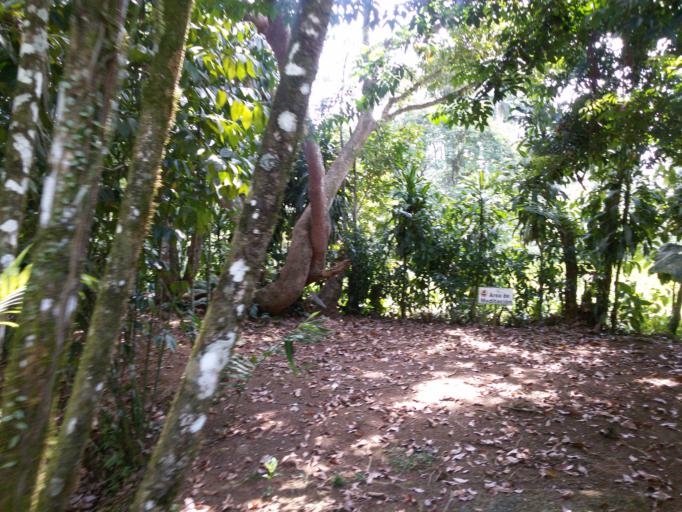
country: CR
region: San Jose
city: Dulce Nombre de Jesus
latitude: 10.3317
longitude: -83.9425
